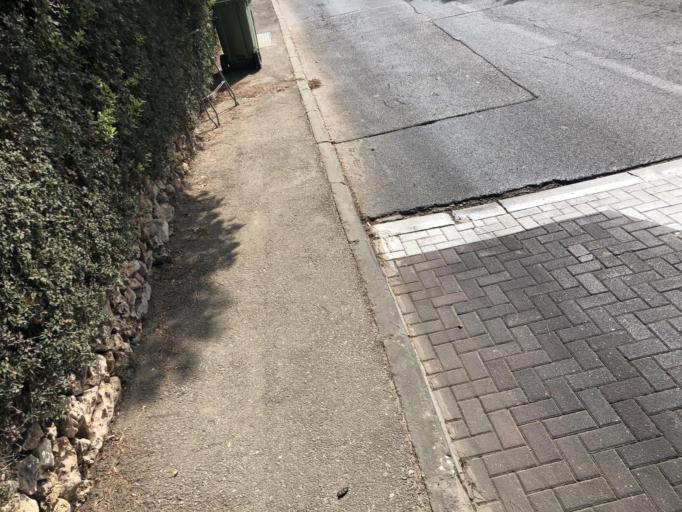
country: PS
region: West Bank
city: Jit
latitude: 32.2139
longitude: 35.1572
